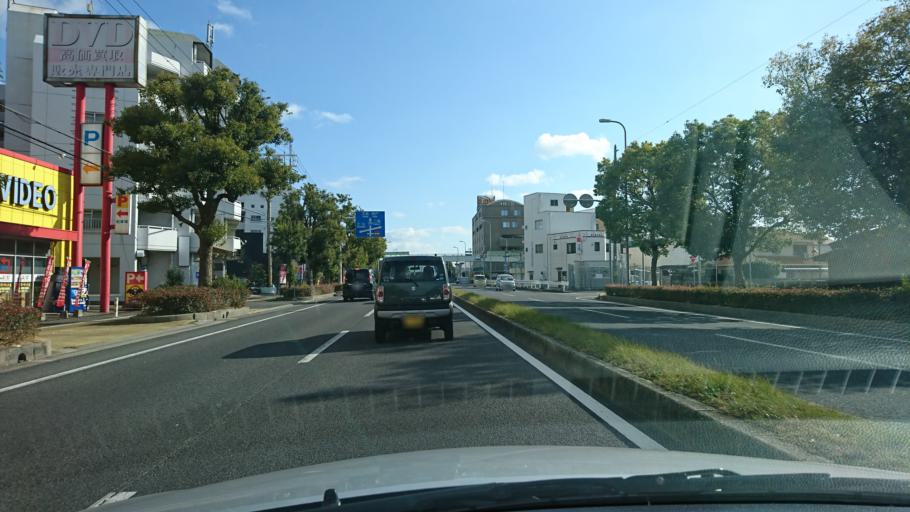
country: JP
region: Hyogo
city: Kakogawacho-honmachi
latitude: 34.7028
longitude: 134.8892
